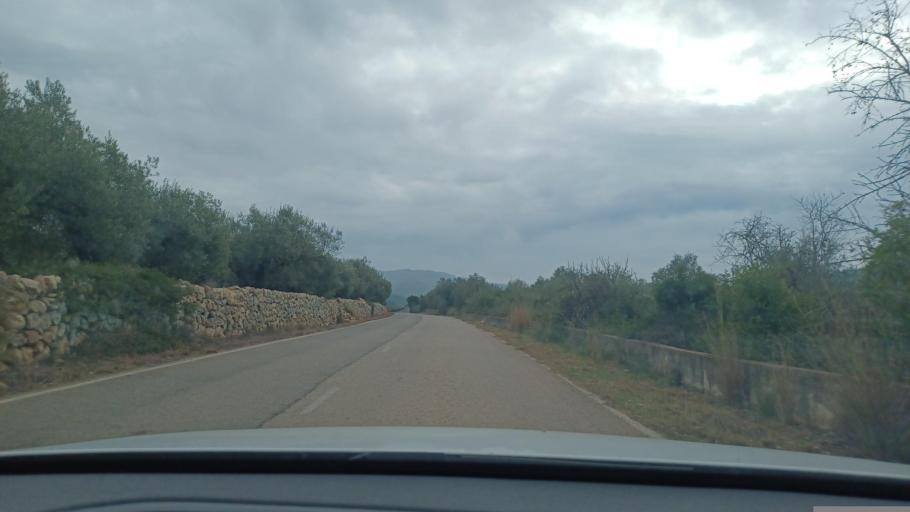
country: ES
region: Catalonia
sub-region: Provincia de Tarragona
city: Santa Barbara
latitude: 40.6646
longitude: 0.4544
